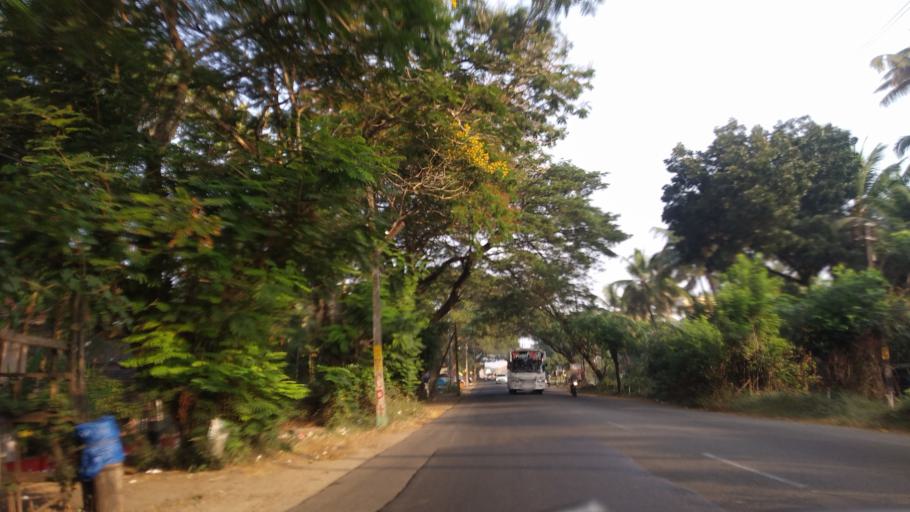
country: IN
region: Kerala
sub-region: Thrissur District
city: Kodungallur
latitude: 10.1904
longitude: 76.2015
